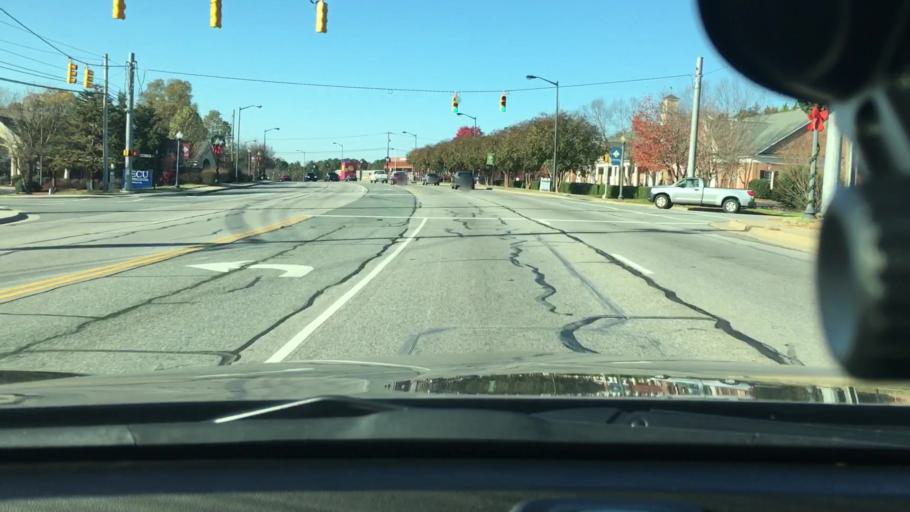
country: US
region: North Carolina
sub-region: Cabarrus County
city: Harrisburg
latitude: 35.3203
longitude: -80.6697
